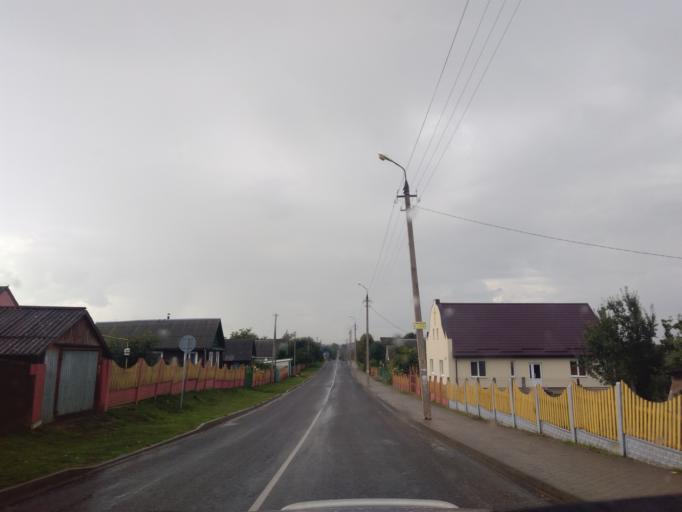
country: BY
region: Minsk
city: Kapyl'
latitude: 53.1535
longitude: 27.0901
